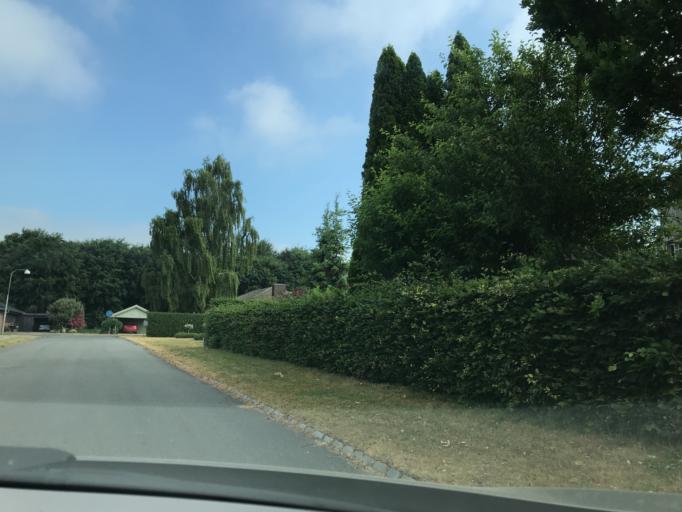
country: DK
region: South Denmark
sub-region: Odense Kommune
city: Bellinge
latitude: 55.3753
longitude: 10.3440
